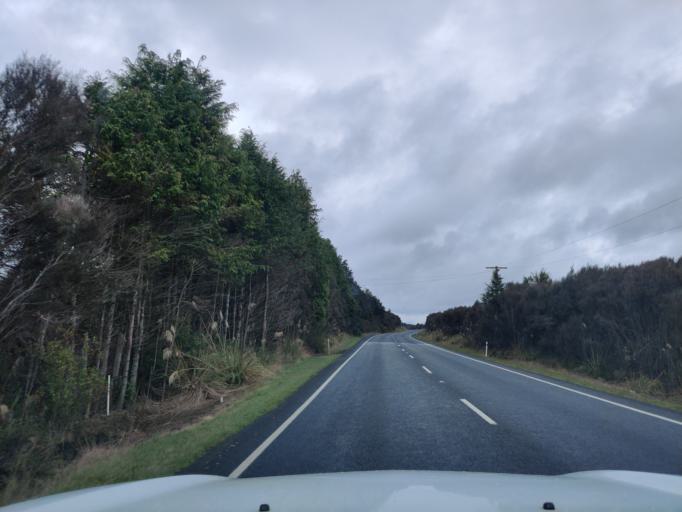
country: NZ
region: Manawatu-Wanganui
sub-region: Ruapehu District
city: Waiouru
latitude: -39.3357
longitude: 175.3799
